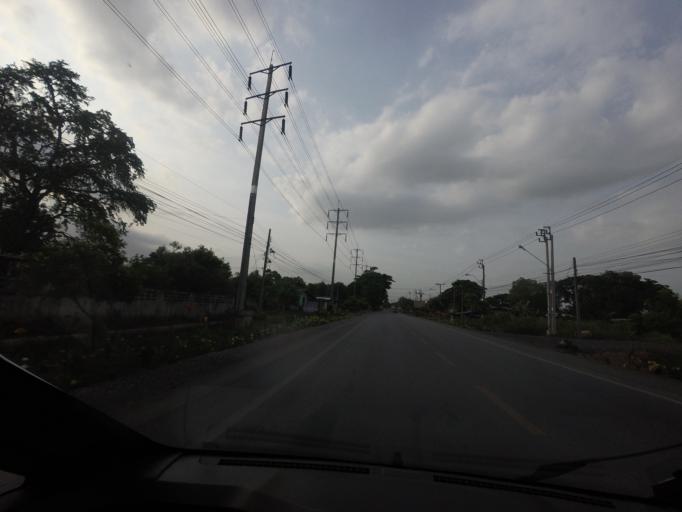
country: TH
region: Bangkok
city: Nong Chok
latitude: 13.8732
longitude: 100.8633
